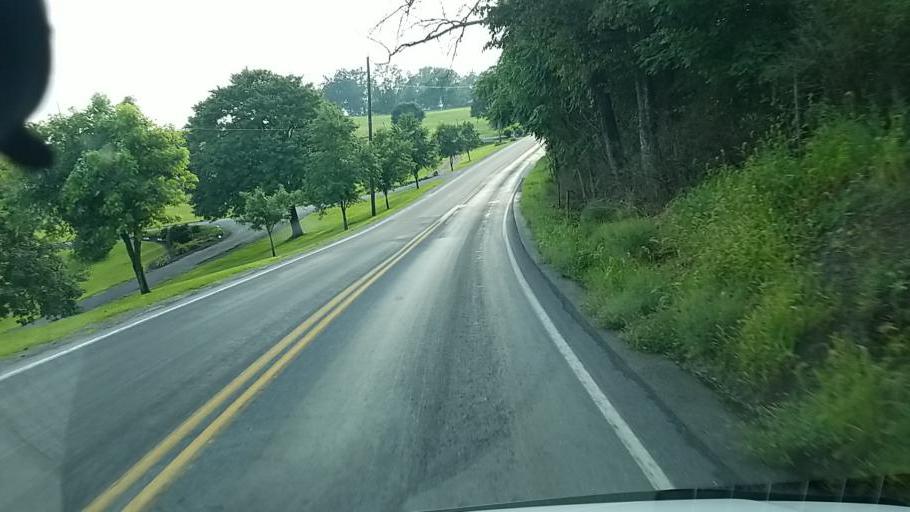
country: US
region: Pennsylvania
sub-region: Cumberland County
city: Newville
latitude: 40.1884
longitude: -77.5172
